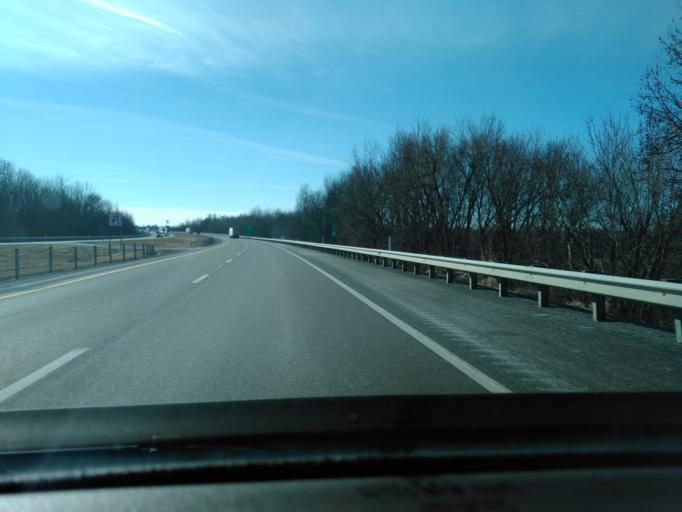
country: US
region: Illinois
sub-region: Massac County
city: Metropolis
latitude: 37.1143
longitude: -88.6934
